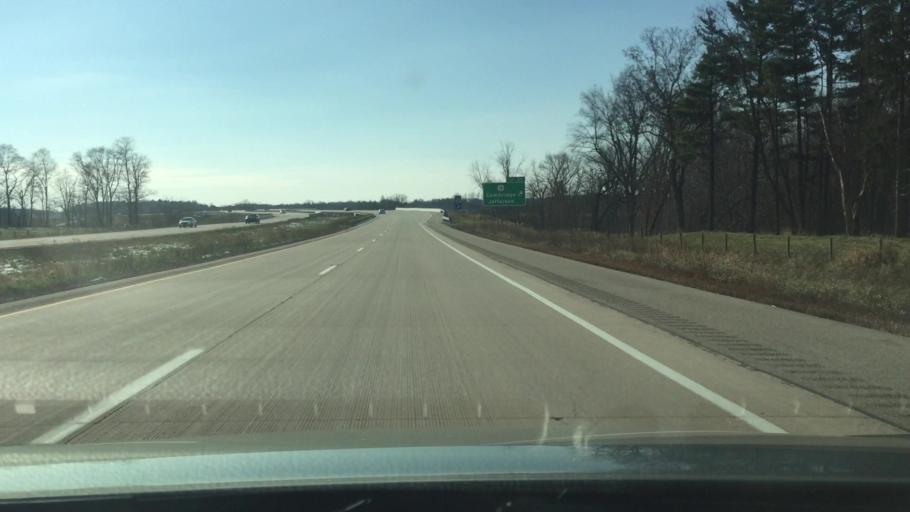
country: US
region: Wisconsin
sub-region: Jefferson County
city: Jefferson
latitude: 43.0113
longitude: -88.8312
